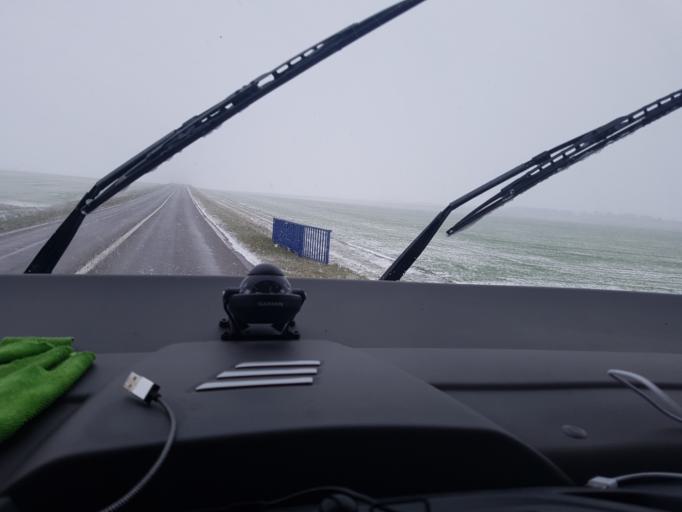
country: FR
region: Lorraine
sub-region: Departement de la Moselle
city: Chateau-Salins
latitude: 48.8779
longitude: 6.4085
